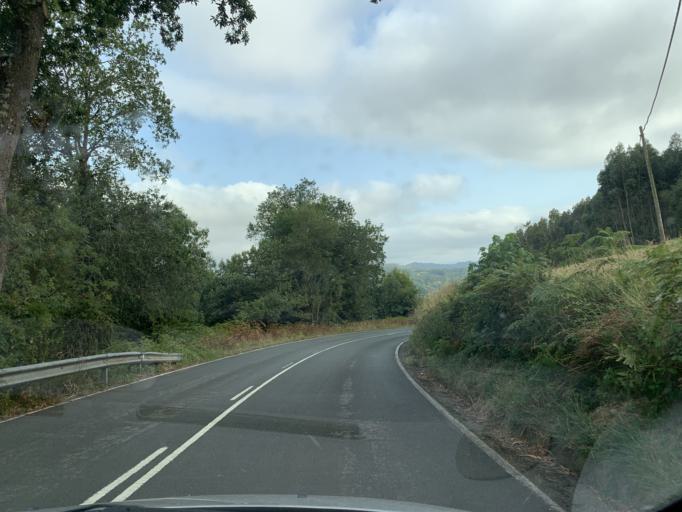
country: ES
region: Asturias
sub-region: Province of Asturias
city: Villaviciosa
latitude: 43.5125
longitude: -5.4267
